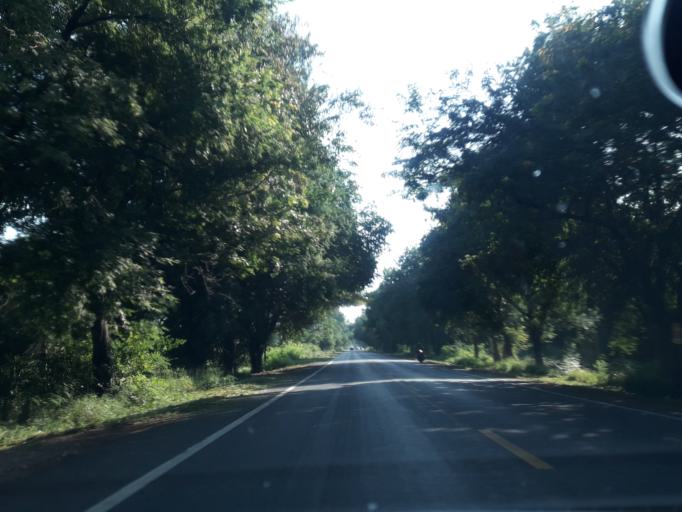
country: TH
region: Sara Buri
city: Phra Phutthabat
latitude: 14.8197
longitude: 100.8385
